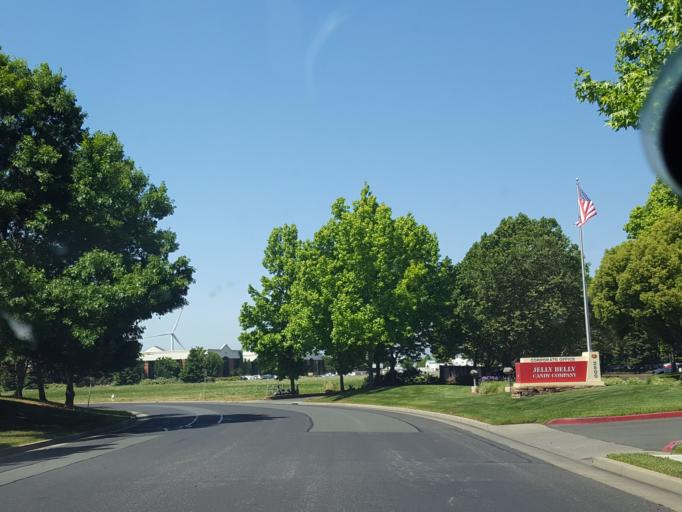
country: US
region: California
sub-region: Solano County
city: Suisun
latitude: 38.2373
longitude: -122.0781
